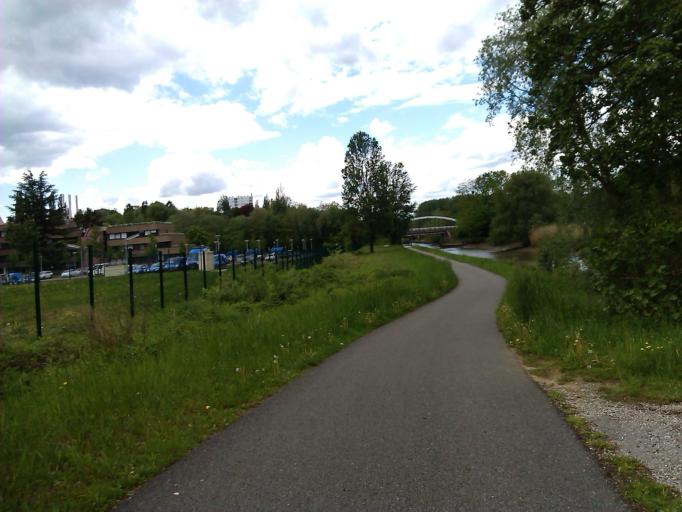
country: FR
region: Franche-Comte
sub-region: Departement du Doubs
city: Arbouans
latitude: 47.5044
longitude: 6.8082
